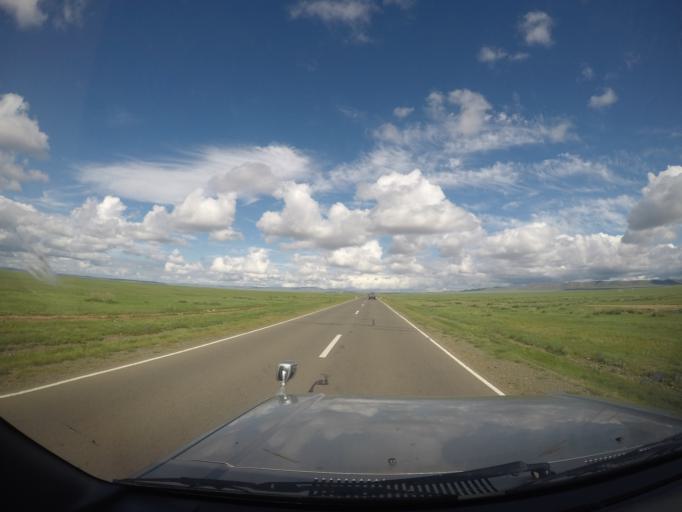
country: MN
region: Hentiy
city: Moron
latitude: 47.4202
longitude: 110.0208
